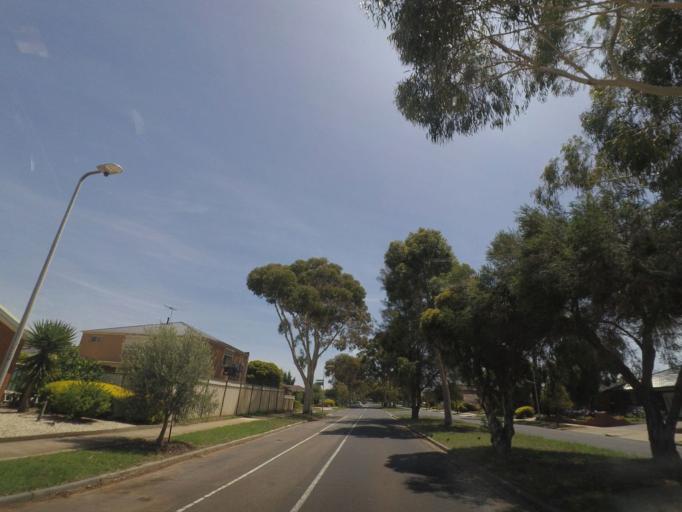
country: AU
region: Victoria
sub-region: Brimbank
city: Keilor Lodge
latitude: -37.7087
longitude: 144.8003
